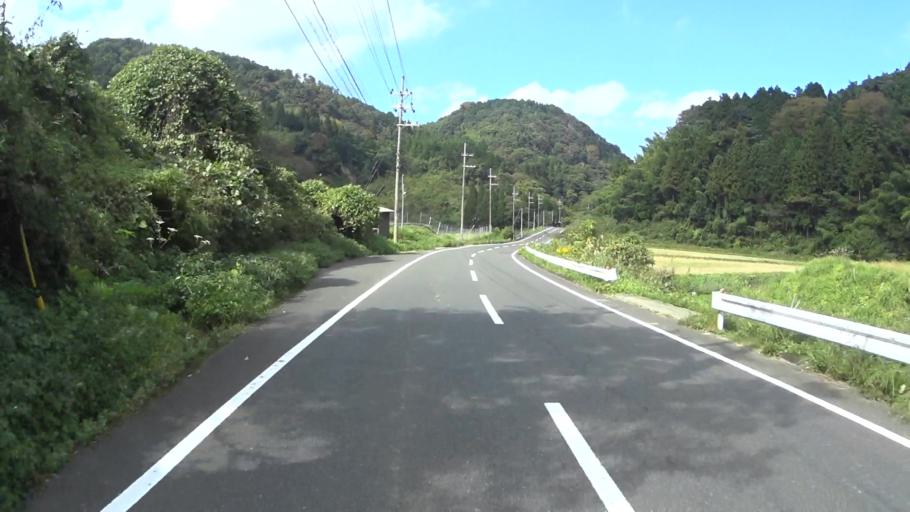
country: JP
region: Kyoto
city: Miyazu
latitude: 35.6907
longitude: 135.2522
